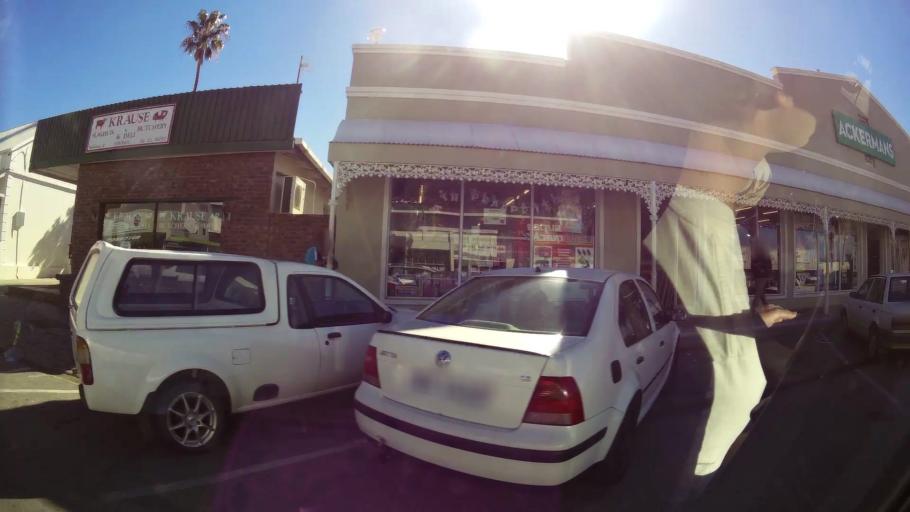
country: ZA
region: Western Cape
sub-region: Cape Winelands District Municipality
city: Ashton
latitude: -33.7862
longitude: 20.1244
